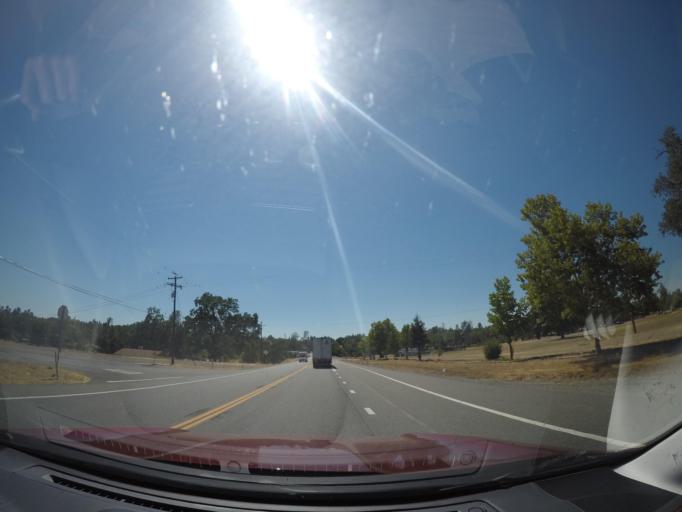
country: US
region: California
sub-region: Shasta County
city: Bella Vista
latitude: 40.6391
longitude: -122.2384
